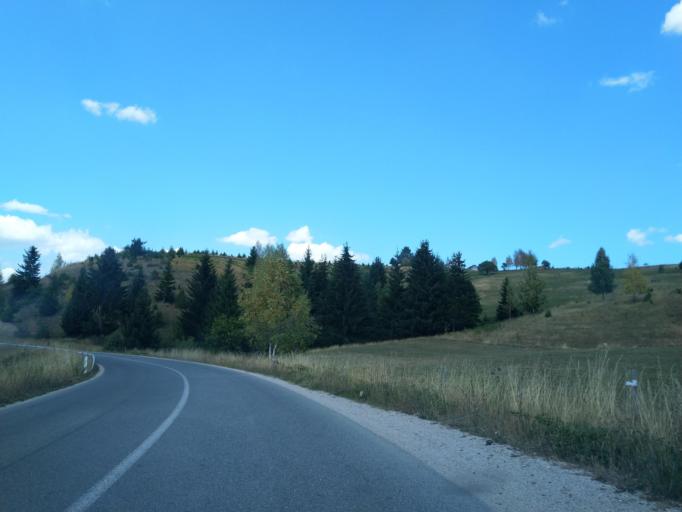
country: RS
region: Central Serbia
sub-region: Zlatiborski Okrug
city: Nova Varos
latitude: 43.4276
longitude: 19.8305
